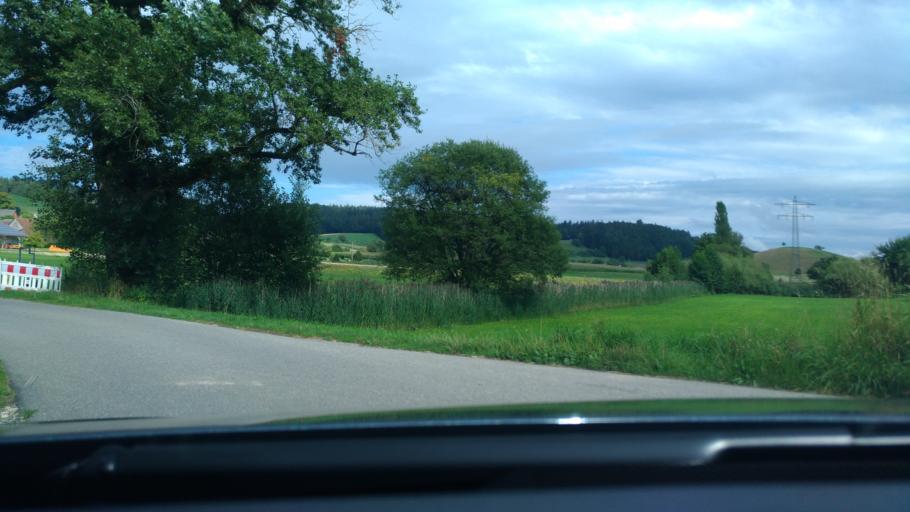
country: DE
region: Baden-Wuerttemberg
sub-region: Tuebingen Region
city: Sipplingen
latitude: 47.8152
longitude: 9.1116
